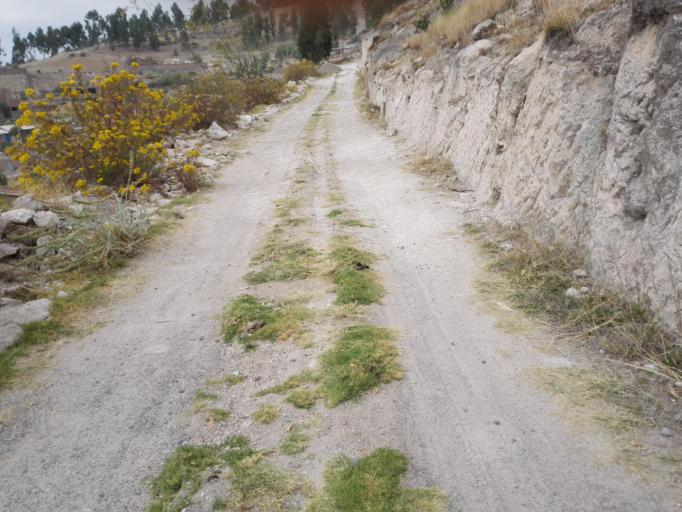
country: PE
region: Ayacucho
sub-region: Provincia de Huamanga
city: Ayacucho
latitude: -13.1470
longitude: -74.2369
